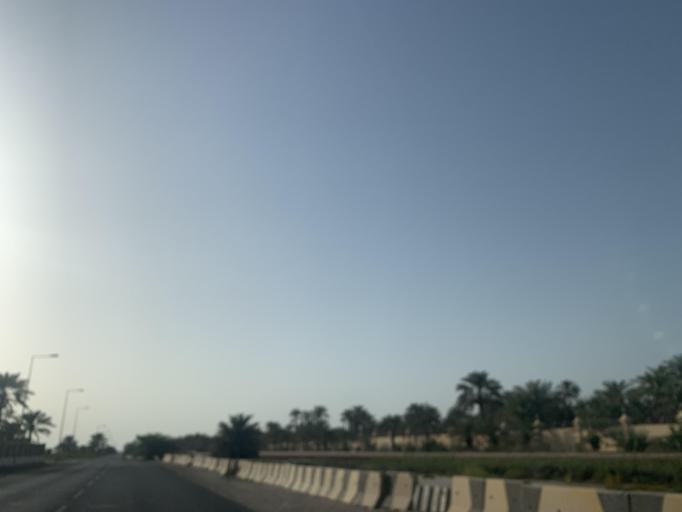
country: BH
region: Central Governorate
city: Madinat Hamad
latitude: 26.1756
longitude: 50.4588
